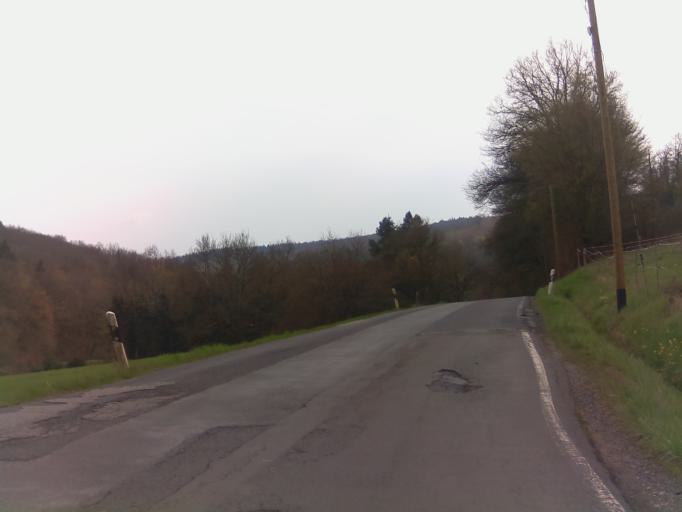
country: DE
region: Rheinland-Pfalz
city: Allenfeld
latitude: 49.8552
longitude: 7.6593
